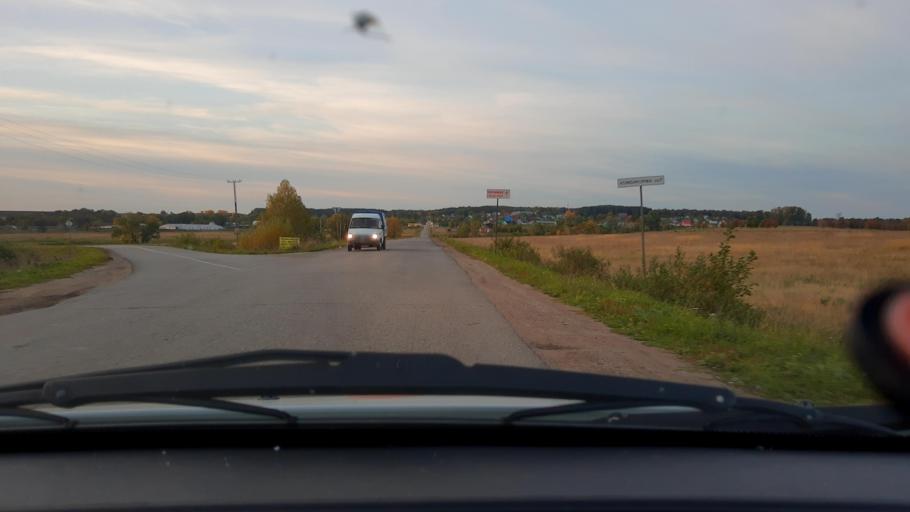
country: RU
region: Bashkortostan
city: Iglino
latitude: 54.7848
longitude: 56.5376
